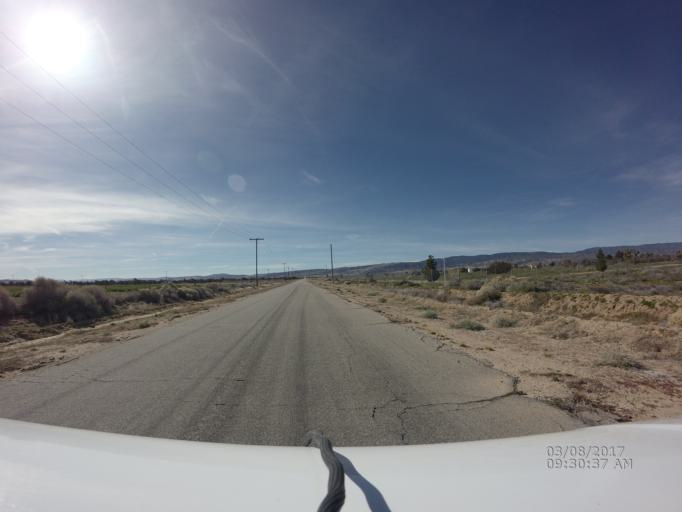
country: US
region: California
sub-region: Los Angeles County
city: Green Valley
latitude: 34.7912
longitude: -118.4666
